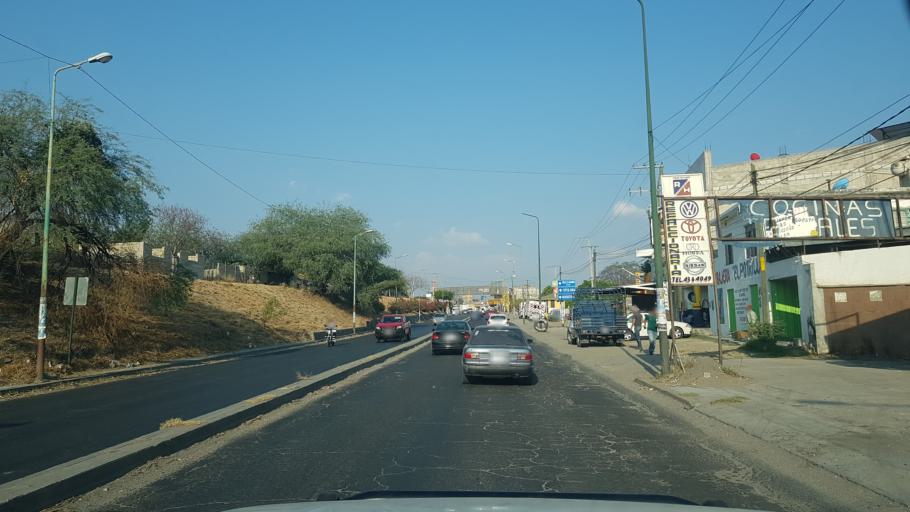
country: MX
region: Puebla
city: Izucar de Matamoros
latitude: 18.6010
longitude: -98.4742
